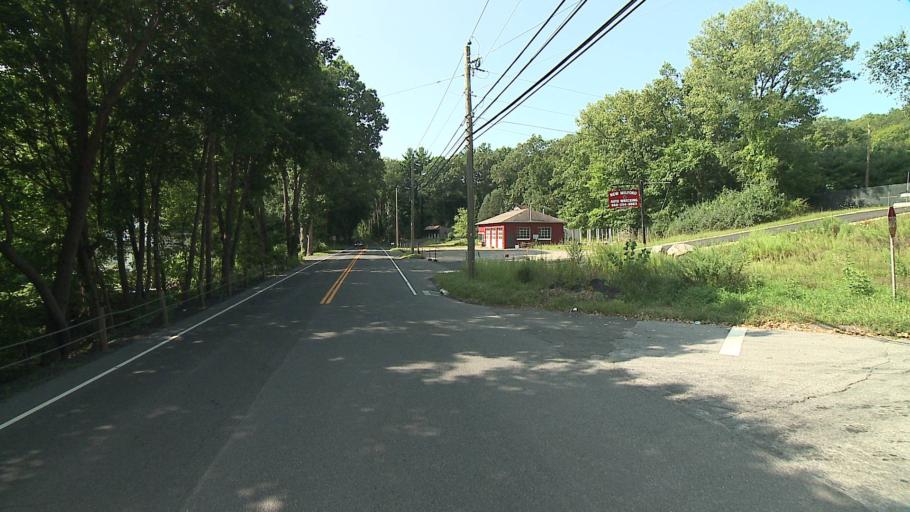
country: US
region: Connecticut
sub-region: Fairfield County
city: Sherman
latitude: 41.6067
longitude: -73.4576
